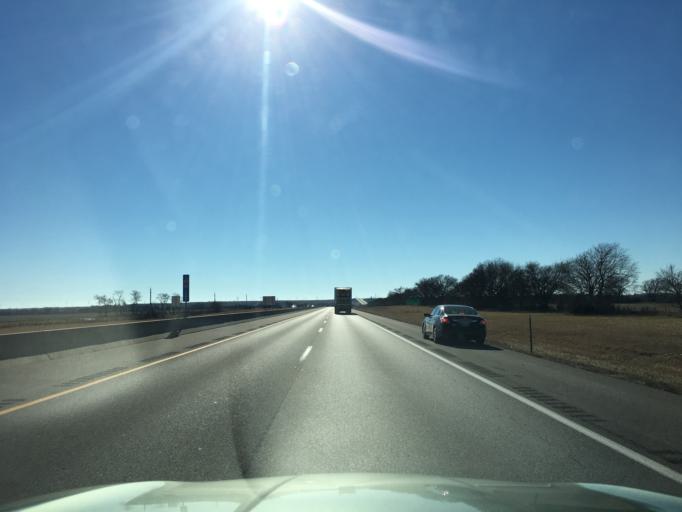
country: US
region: Kansas
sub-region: Sumner County
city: Wellington
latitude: 37.2277
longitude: -97.3389
